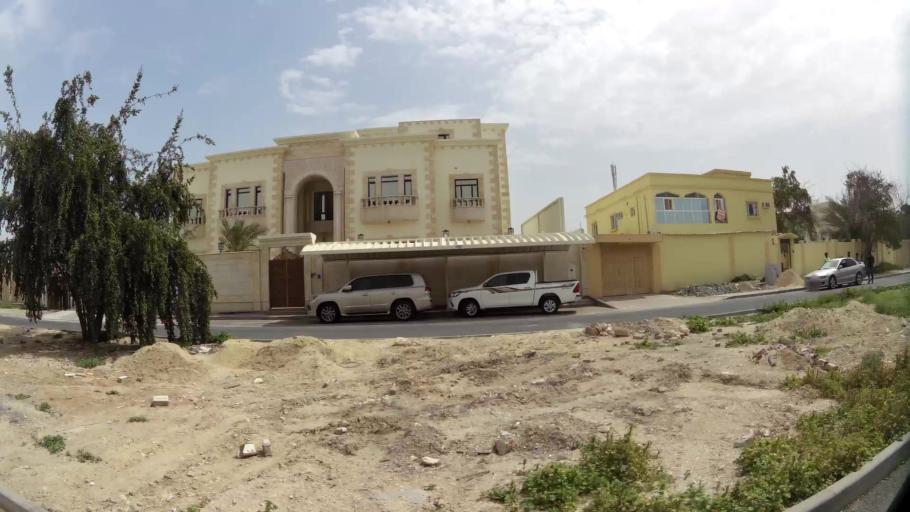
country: QA
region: Baladiyat ad Dawhah
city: Doha
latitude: 25.3100
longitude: 51.4837
